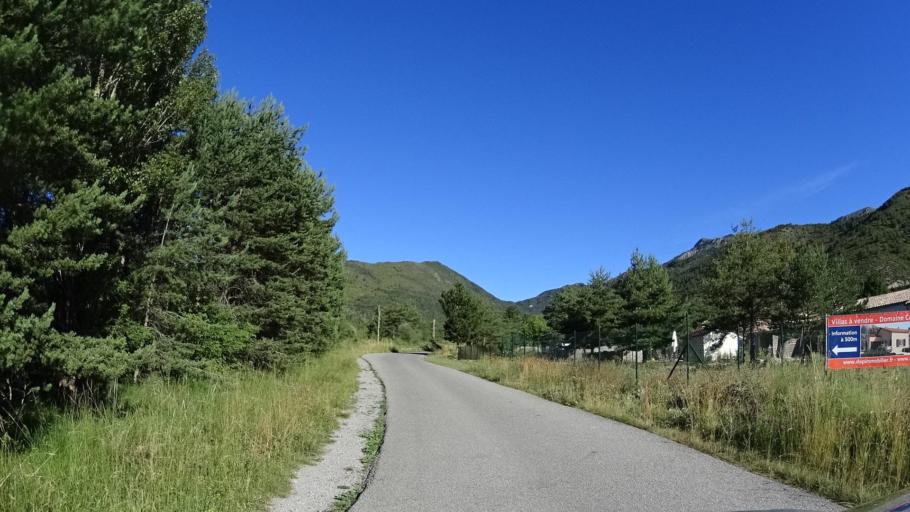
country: FR
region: Provence-Alpes-Cote d'Azur
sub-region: Departement des Alpes-de-Haute-Provence
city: Castellane
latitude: 43.8765
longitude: 6.5074
